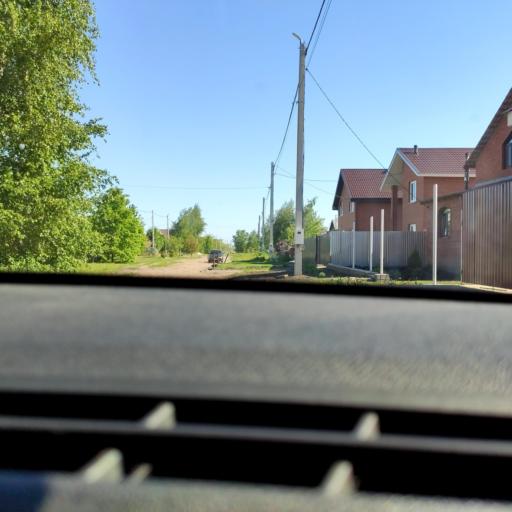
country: RU
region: Samara
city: Tol'yatti
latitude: 53.5586
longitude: 49.4097
